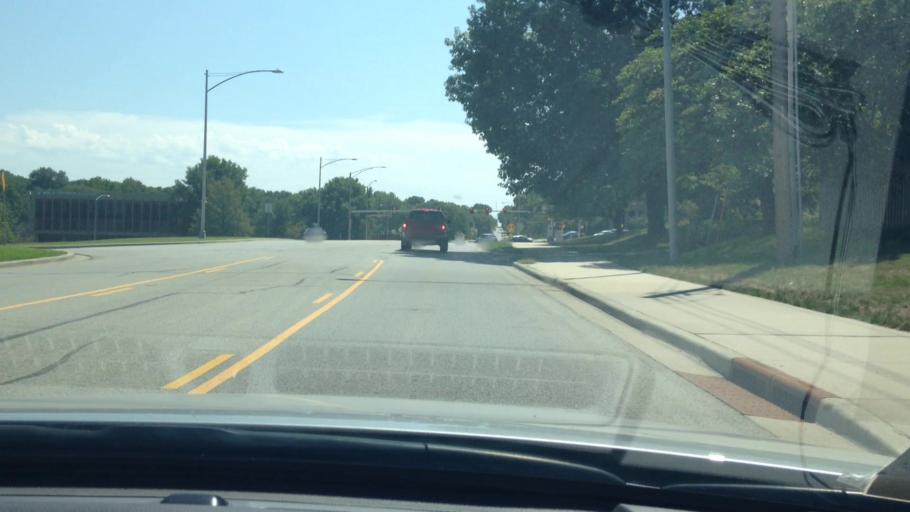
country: US
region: Kansas
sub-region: Johnson County
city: Mission
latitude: 39.0175
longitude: -94.6491
